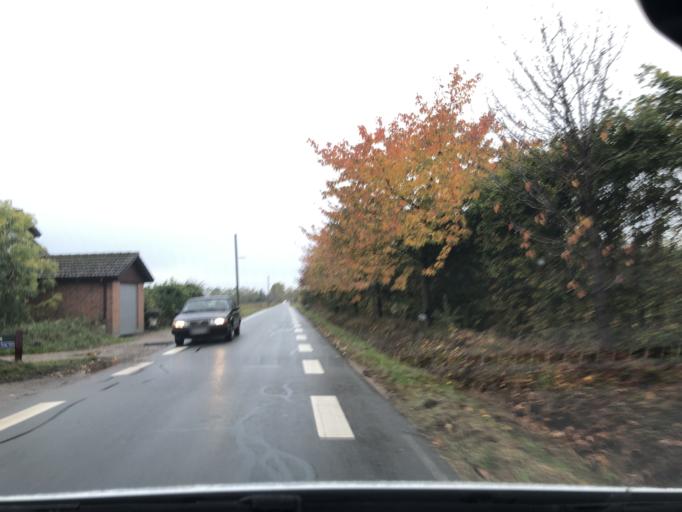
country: DK
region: Capital Region
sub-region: Tarnby Kommune
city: Tarnby
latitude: 55.5698
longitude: 12.5911
